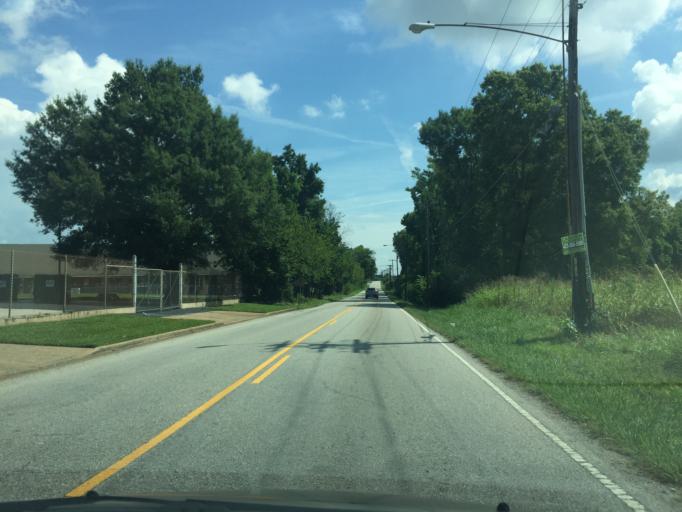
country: US
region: Tennessee
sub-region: Hamilton County
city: East Chattanooga
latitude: 35.0605
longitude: -85.2735
